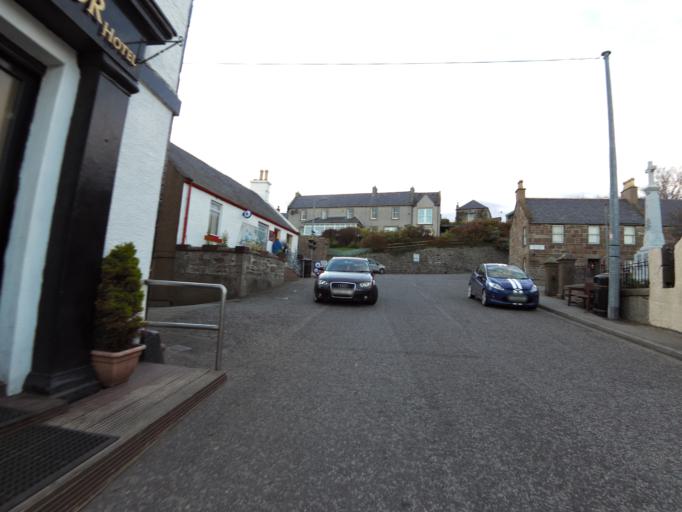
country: GB
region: Scotland
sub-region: Aberdeenshire
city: Inverbervie
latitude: 56.7945
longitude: -2.3364
